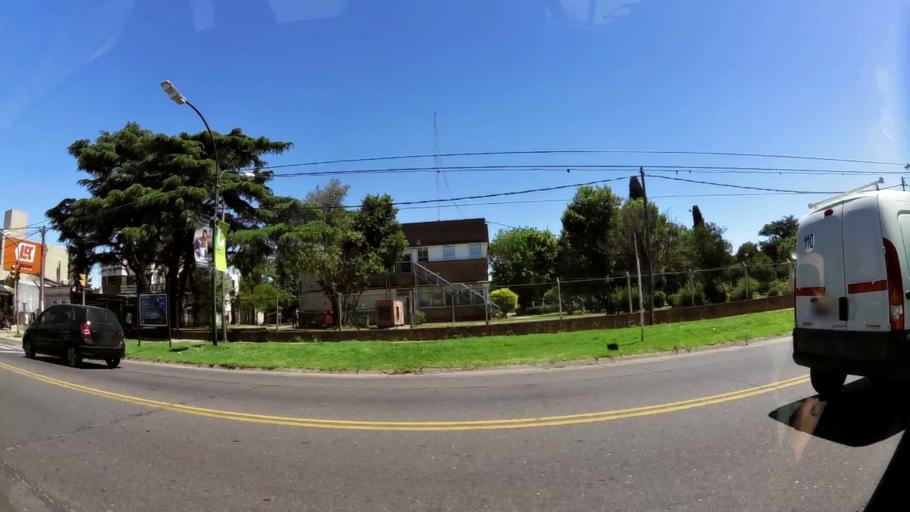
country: AR
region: Buenos Aires
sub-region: Partido de San Isidro
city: San Isidro
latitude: -34.4961
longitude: -58.5209
